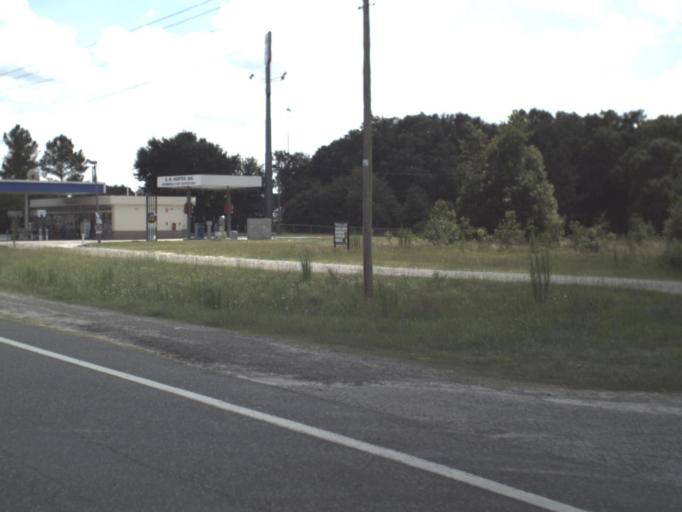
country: US
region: Florida
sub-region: Alachua County
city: High Springs
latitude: 30.0025
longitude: -82.5975
